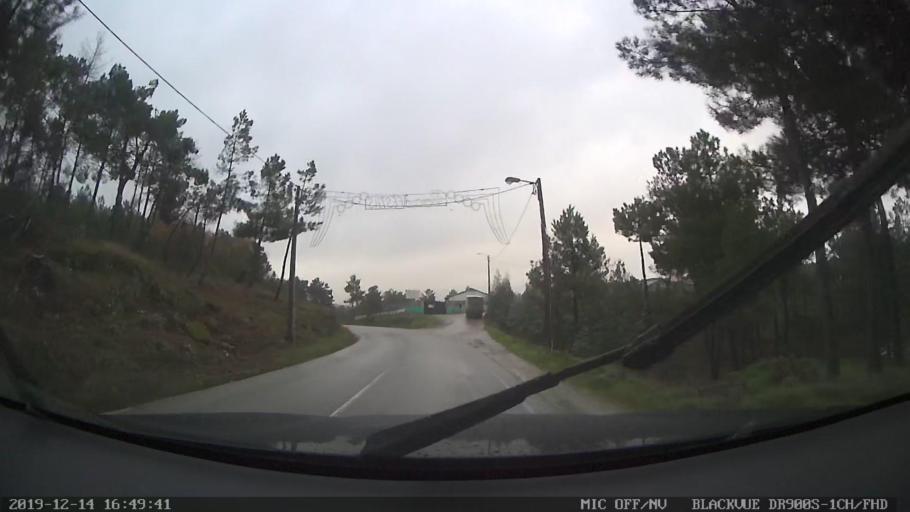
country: PT
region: Vila Real
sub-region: Murca
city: Murca
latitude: 41.4107
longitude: -7.4998
